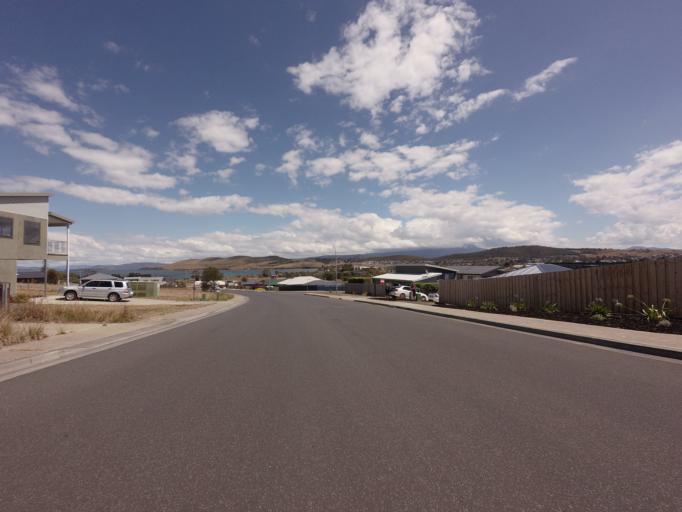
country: AU
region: Tasmania
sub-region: Clarence
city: Rokeby
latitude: -42.9046
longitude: 147.4569
